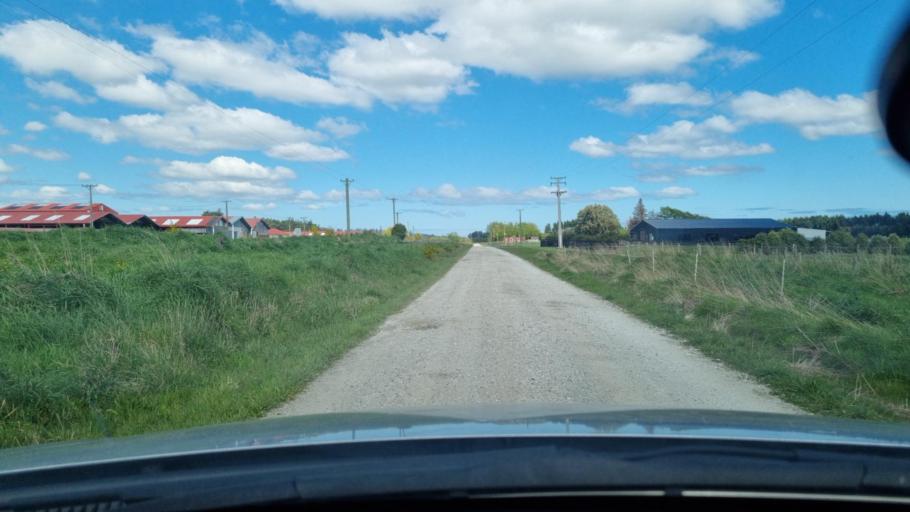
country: NZ
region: Southland
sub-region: Invercargill City
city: Invercargill
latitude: -46.3447
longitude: 168.3401
